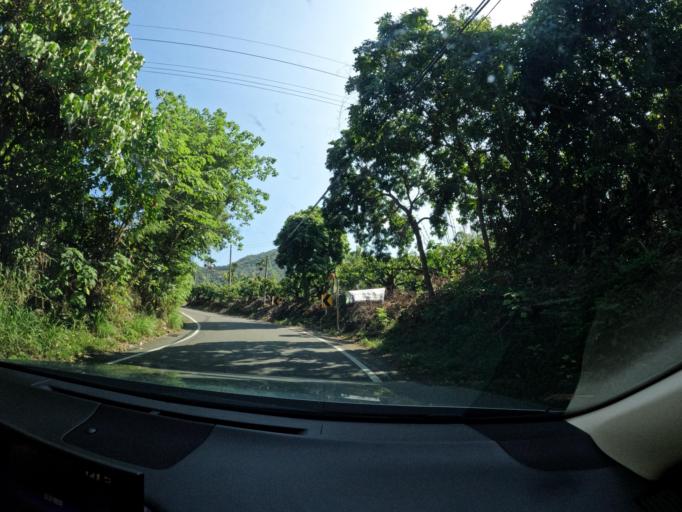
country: TW
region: Taiwan
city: Yujing
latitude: 23.1096
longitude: 120.7113
